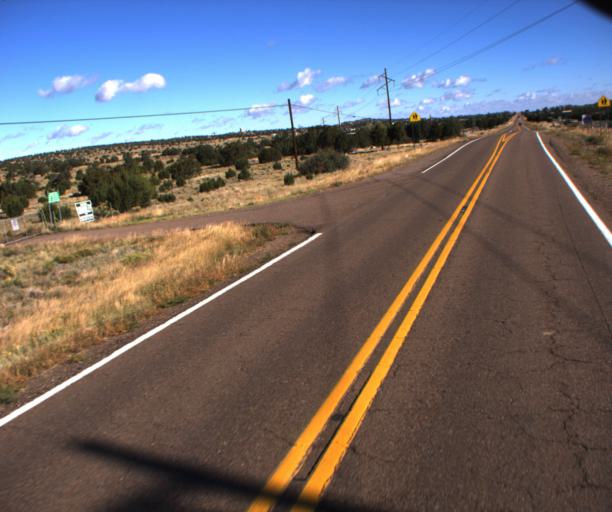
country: US
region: Arizona
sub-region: Apache County
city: Saint Johns
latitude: 34.4219
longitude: -109.6420
